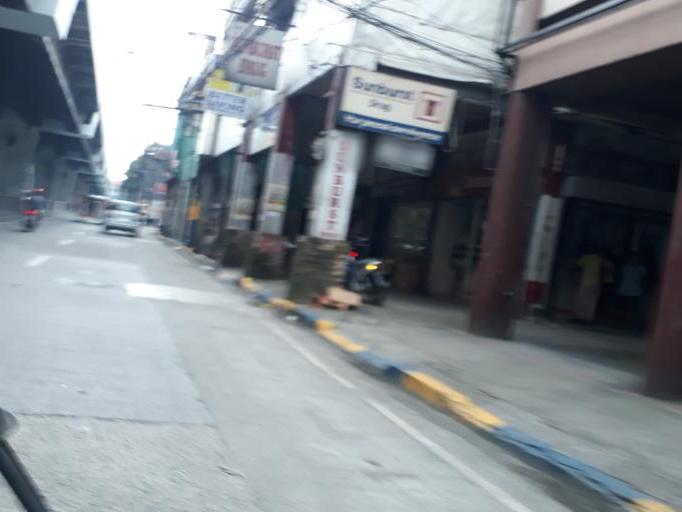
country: PH
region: Metro Manila
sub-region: City of Manila
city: Manila
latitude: 14.6133
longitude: 120.9828
